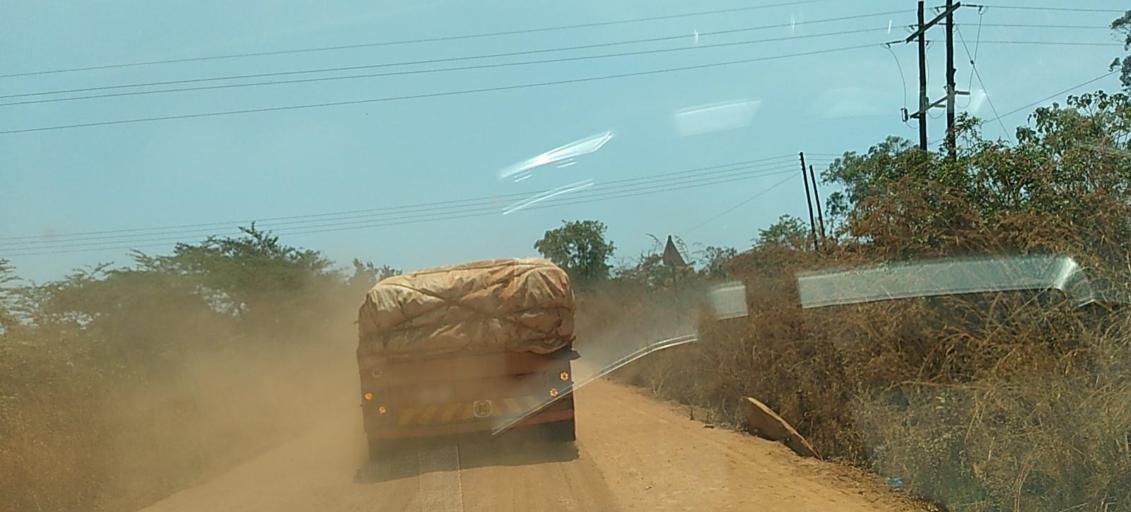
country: CD
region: Katanga
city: Kipushi
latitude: -11.8590
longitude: 27.1183
